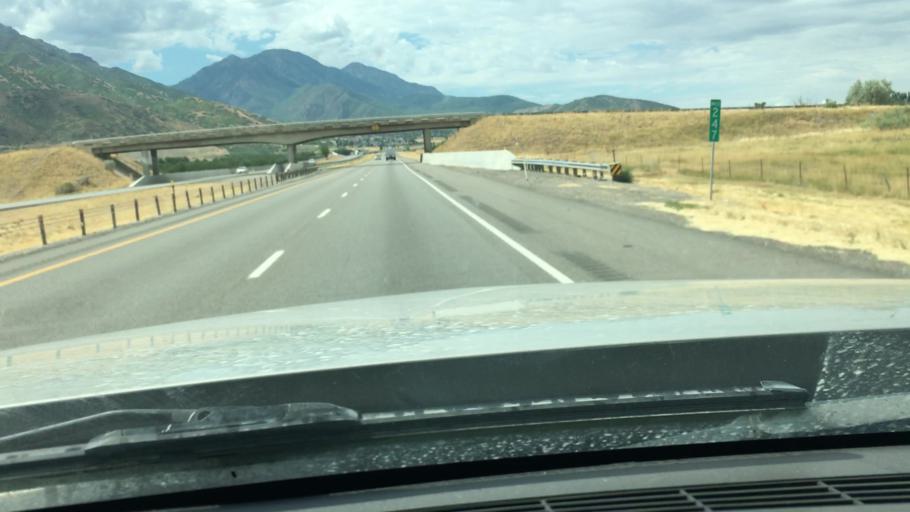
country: US
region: Utah
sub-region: Utah County
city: Santaquin
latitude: 40.0058
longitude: -111.7627
